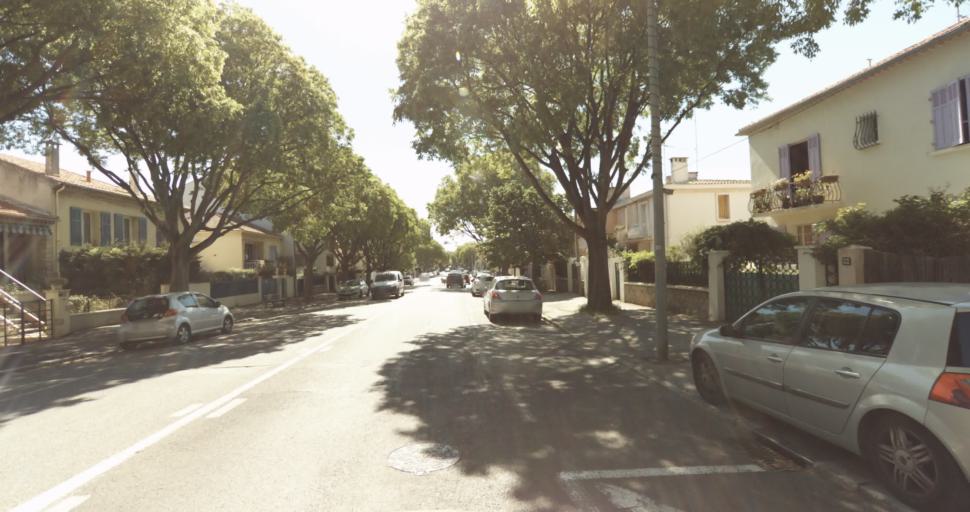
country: FR
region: Provence-Alpes-Cote d'Azur
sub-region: Departement du Var
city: Six-Fours-les-Plages
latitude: 43.1059
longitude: 5.8673
